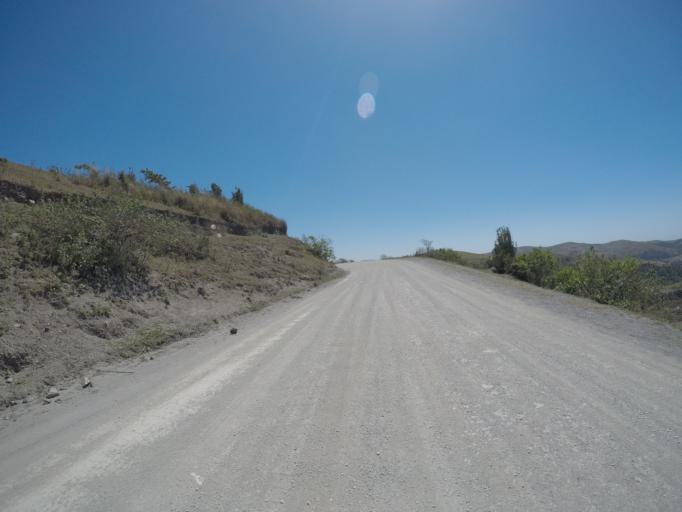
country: ZA
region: Eastern Cape
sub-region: OR Tambo District Municipality
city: Libode
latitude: -31.9987
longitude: 29.0666
